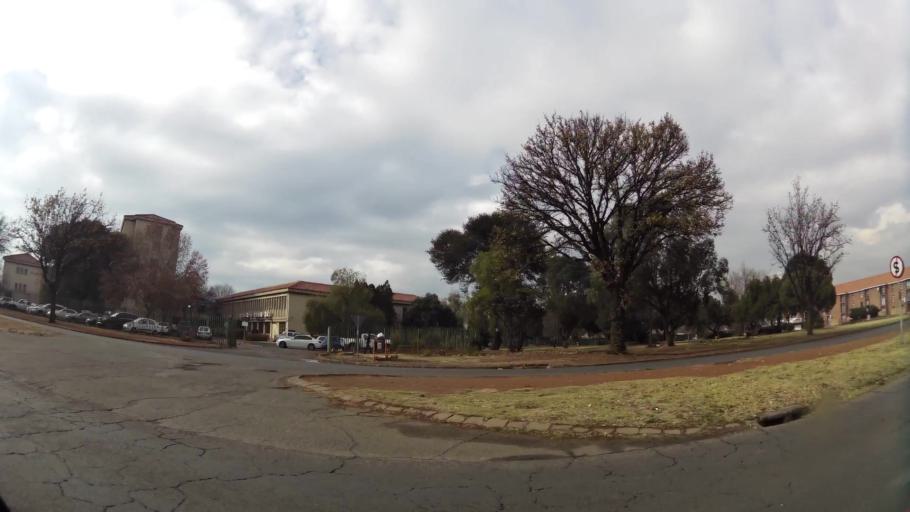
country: ZA
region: Gauteng
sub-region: Sedibeng District Municipality
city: Vanderbijlpark
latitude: -26.6943
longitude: 27.8342
